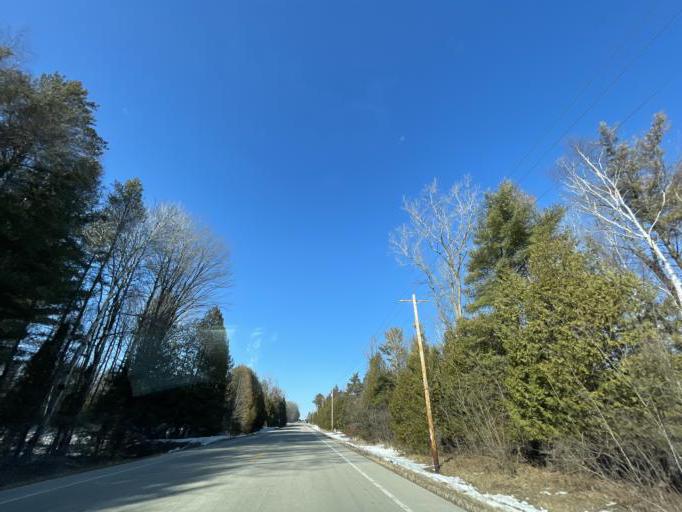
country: US
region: Wisconsin
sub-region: Brown County
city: Suamico
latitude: 44.6498
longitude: -88.0902
